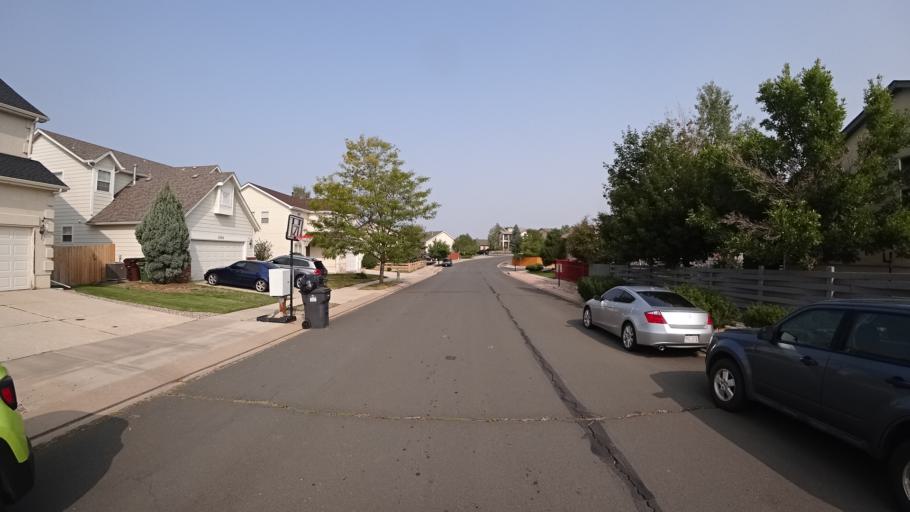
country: US
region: Colorado
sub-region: El Paso County
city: Cimarron Hills
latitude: 38.9290
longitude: -104.7386
